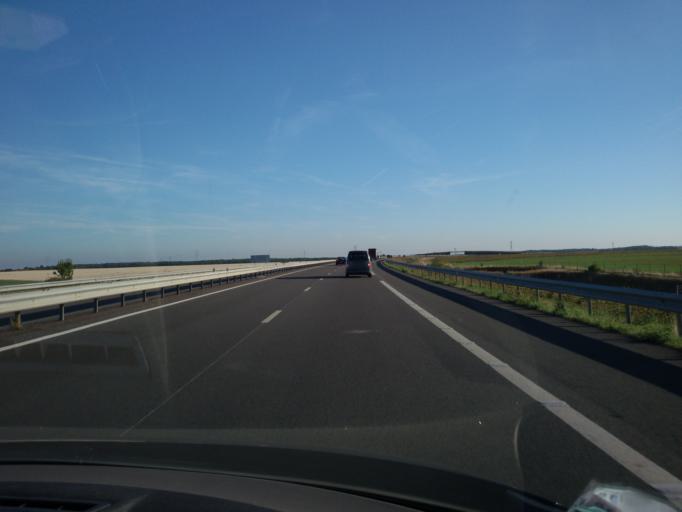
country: FR
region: Centre
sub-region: Departement du Cher
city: Levet
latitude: 46.9530
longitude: 2.4172
